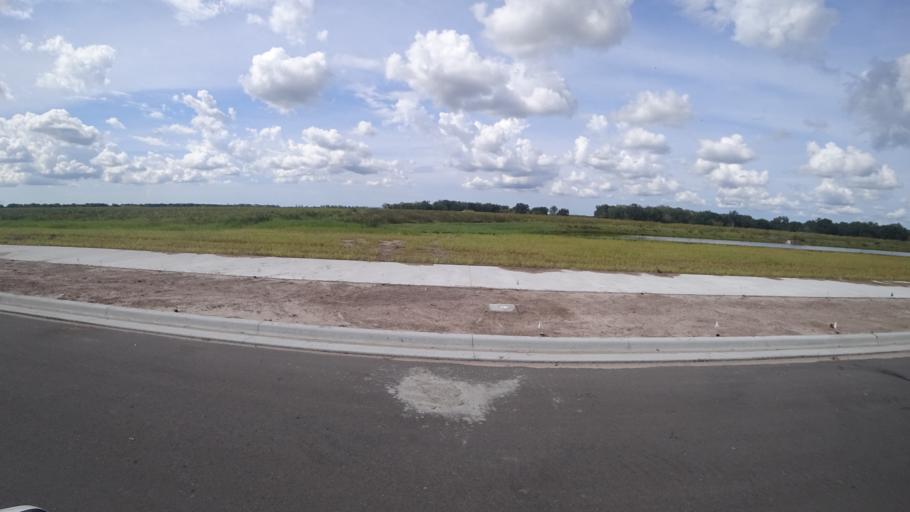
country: US
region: Florida
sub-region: Sarasota County
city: The Meadows
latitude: 27.4542
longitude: -82.3510
